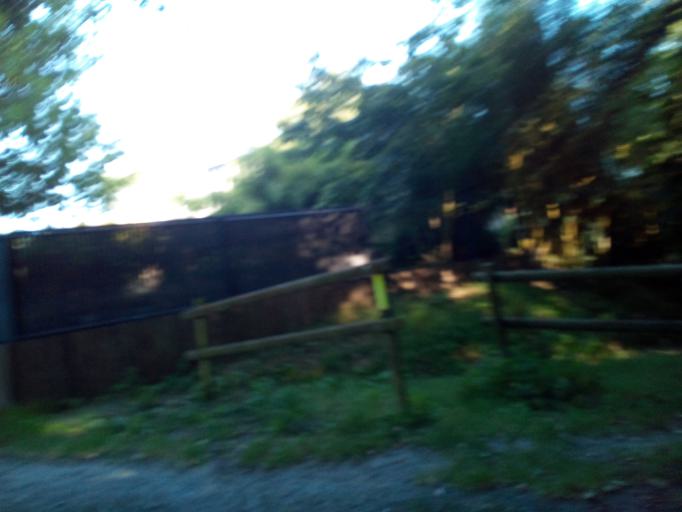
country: FR
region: Brittany
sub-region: Departement du Finistere
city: Landivisiau
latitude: 48.5074
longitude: -4.0841
